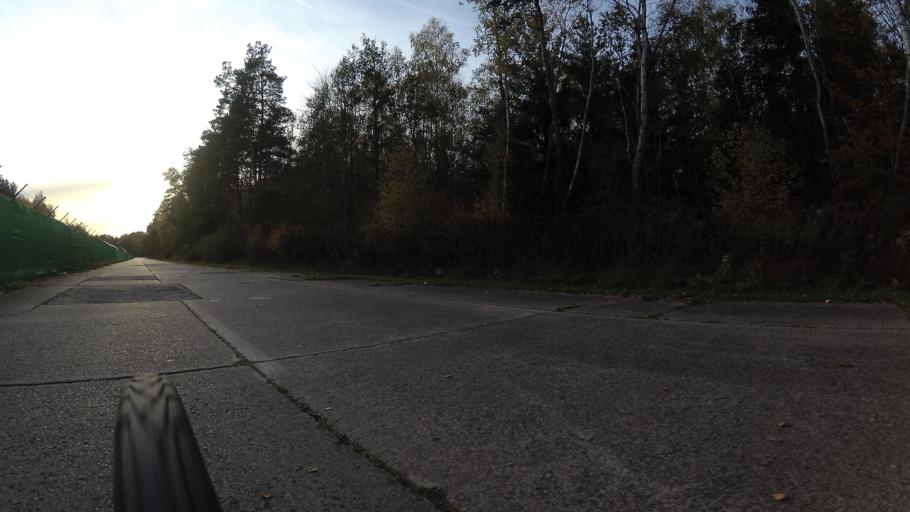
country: DE
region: Rheinland-Pfalz
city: Steinwenden
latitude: 49.4235
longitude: 7.5363
